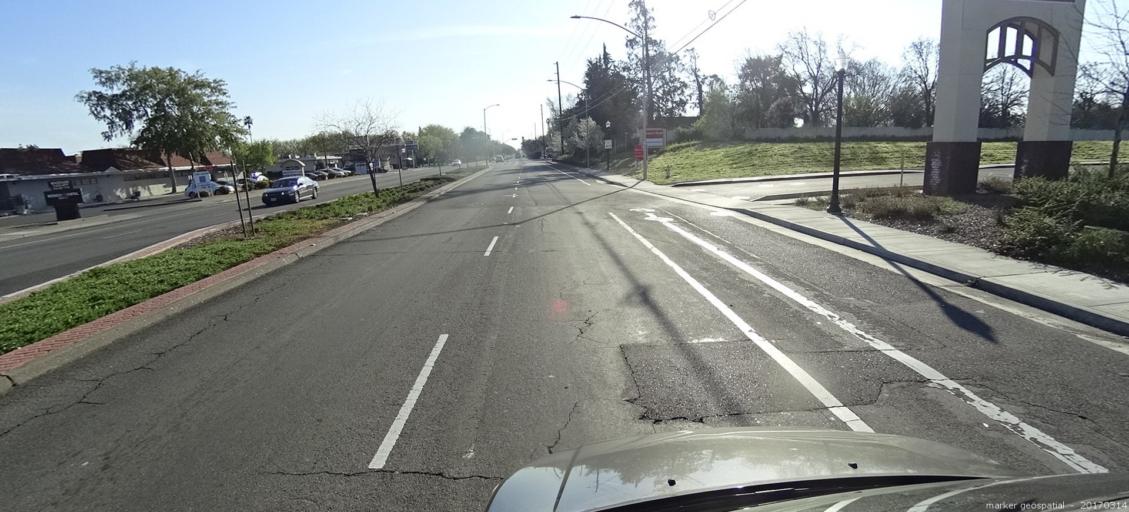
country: US
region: California
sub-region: Sacramento County
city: Parkway
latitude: 38.4956
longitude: -121.5053
